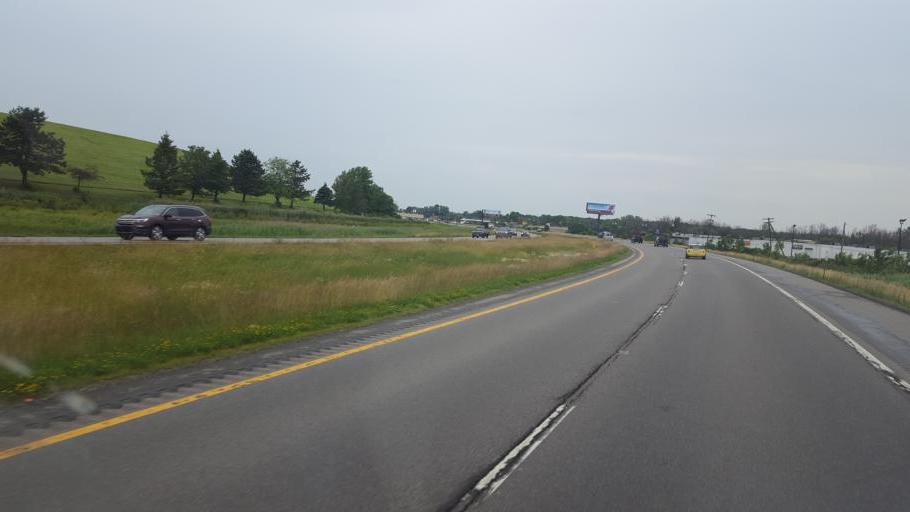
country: US
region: New York
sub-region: Niagara County
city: Niagara Falls
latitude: 43.1005
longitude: -78.9817
